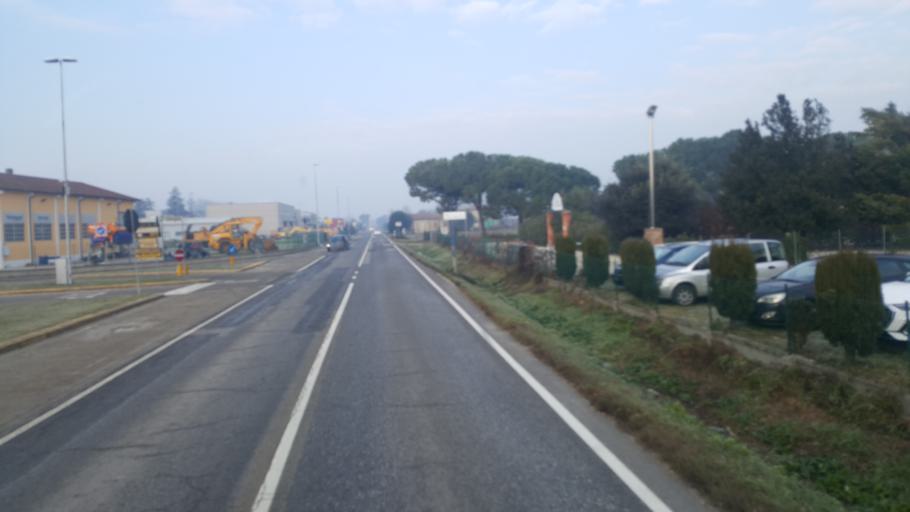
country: IT
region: Emilia-Romagna
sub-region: Provincia di Ravenna
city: Bagnacavallo
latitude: 44.4090
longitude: 11.9964
